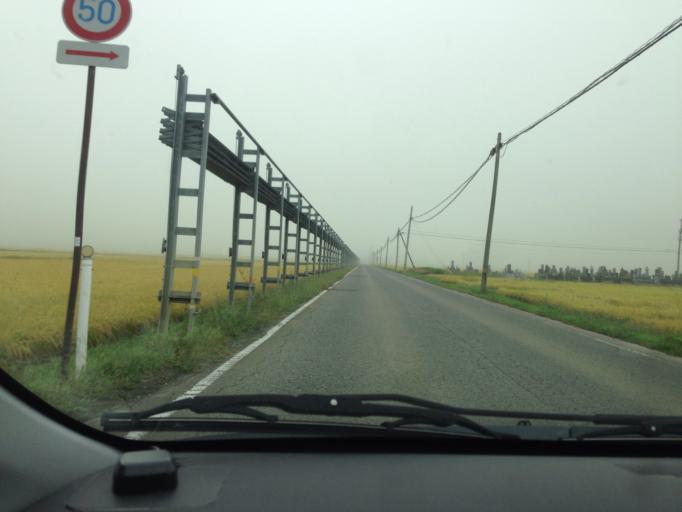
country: JP
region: Fukushima
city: Kitakata
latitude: 37.5581
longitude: 139.8535
